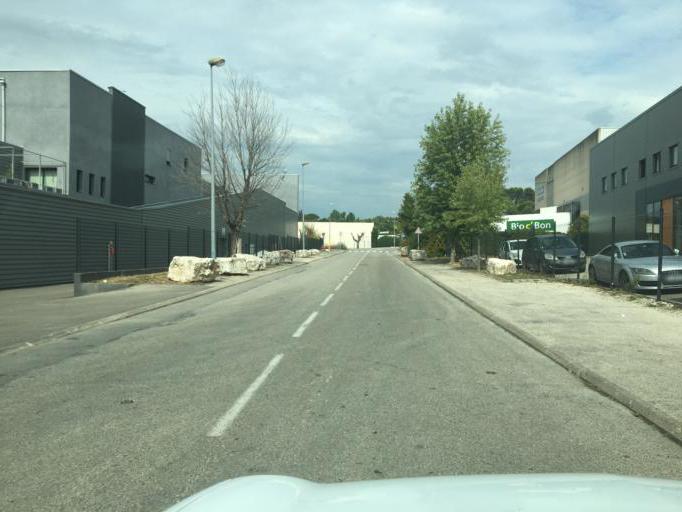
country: FR
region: Provence-Alpes-Cote d'Azur
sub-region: Departement des Bouches-du-Rhone
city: Bouc-Bel-Air
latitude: 43.4863
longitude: 5.3867
